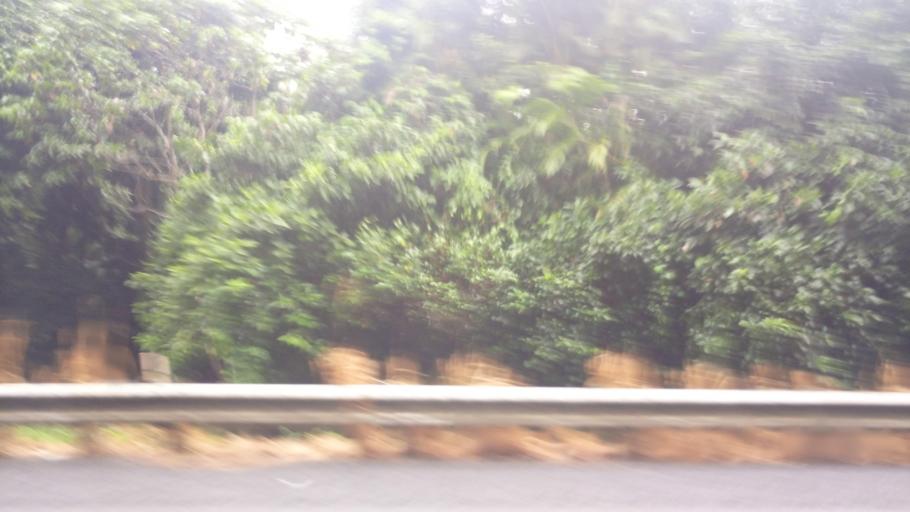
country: AU
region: Queensland
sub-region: Tablelands
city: Ravenshoe
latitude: -17.5982
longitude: 145.7573
